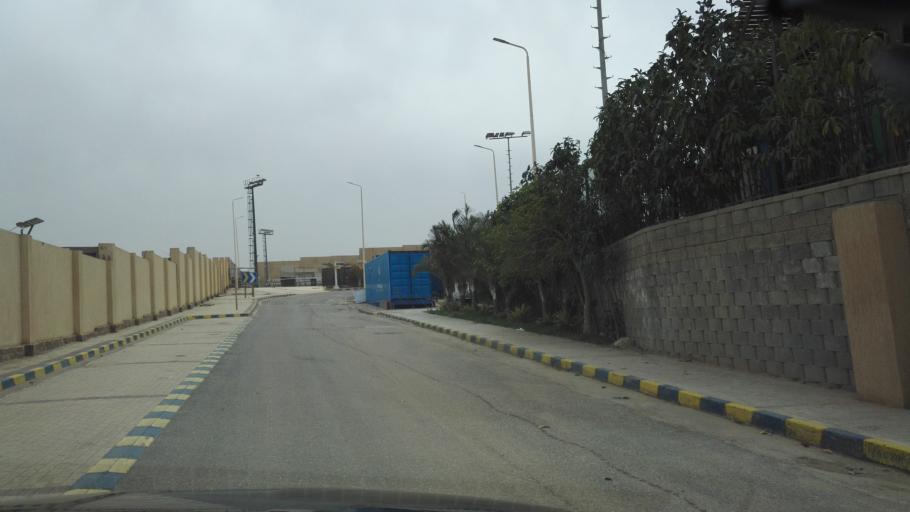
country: EG
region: Muhafazat al Qalyubiyah
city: Al Khankah
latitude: 30.0395
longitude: 31.5293
